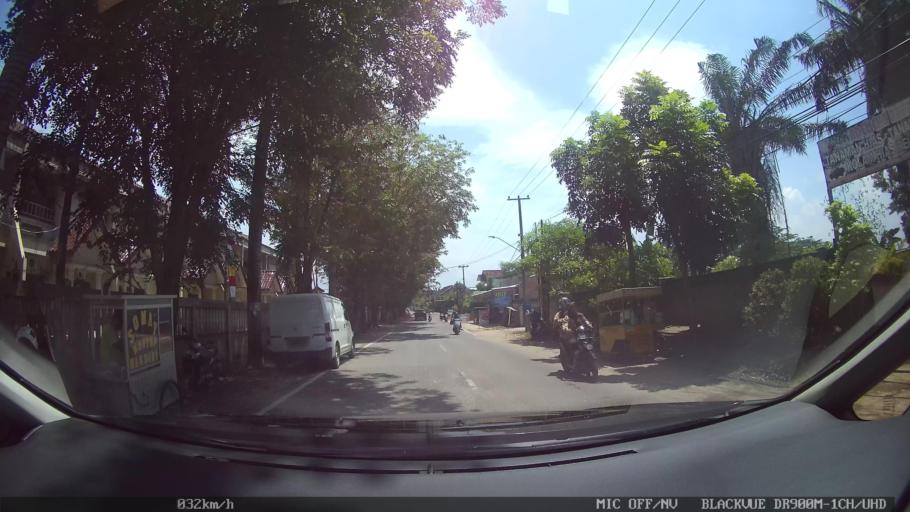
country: ID
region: Lampung
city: Kedaton
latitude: -5.3695
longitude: 105.2898
